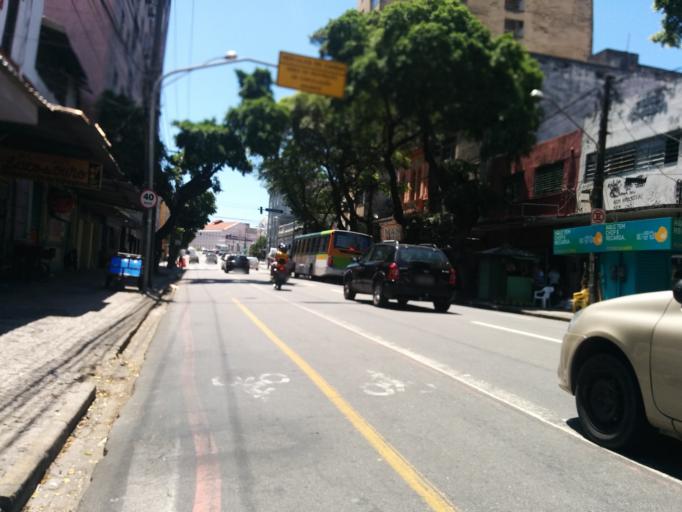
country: BR
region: Pernambuco
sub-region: Recife
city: Recife
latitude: -8.0587
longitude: -34.8812
